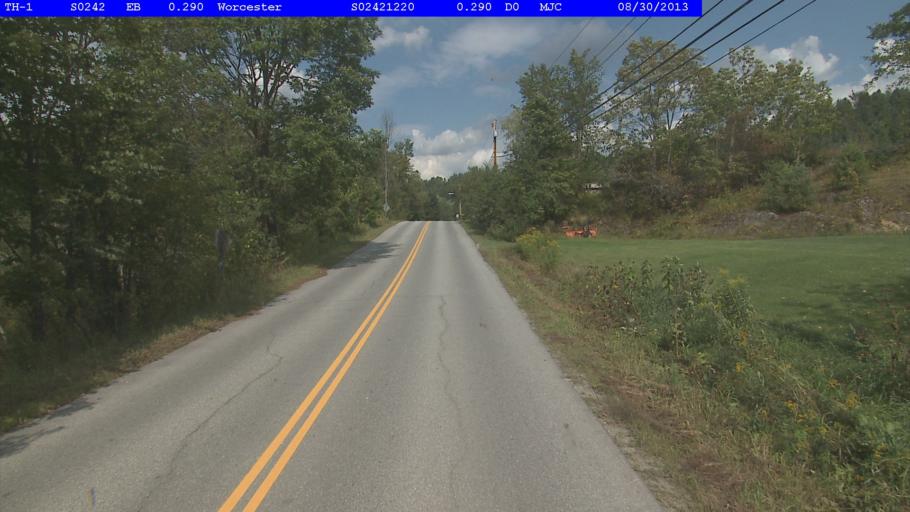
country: US
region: Vermont
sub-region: Washington County
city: Montpelier
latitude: 44.3730
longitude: -72.5446
